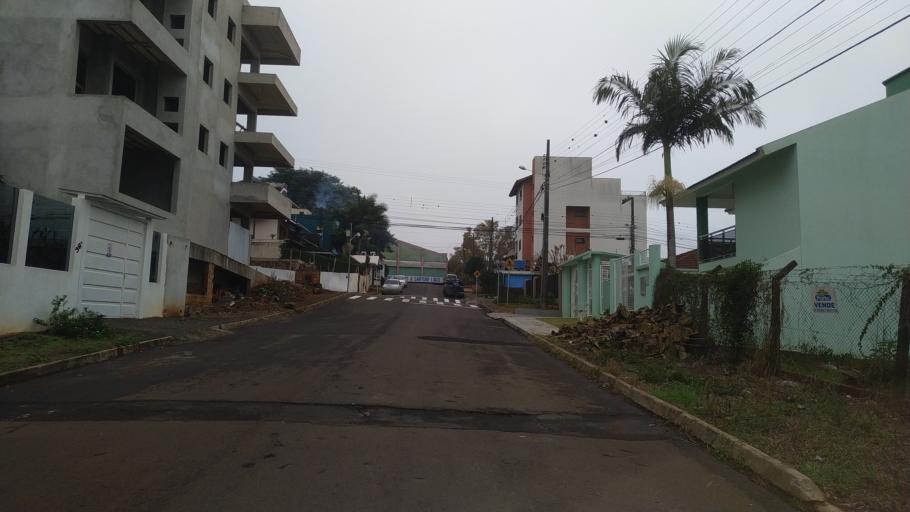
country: BR
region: Santa Catarina
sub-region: Chapeco
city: Chapeco
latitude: -27.0788
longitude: -52.6282
